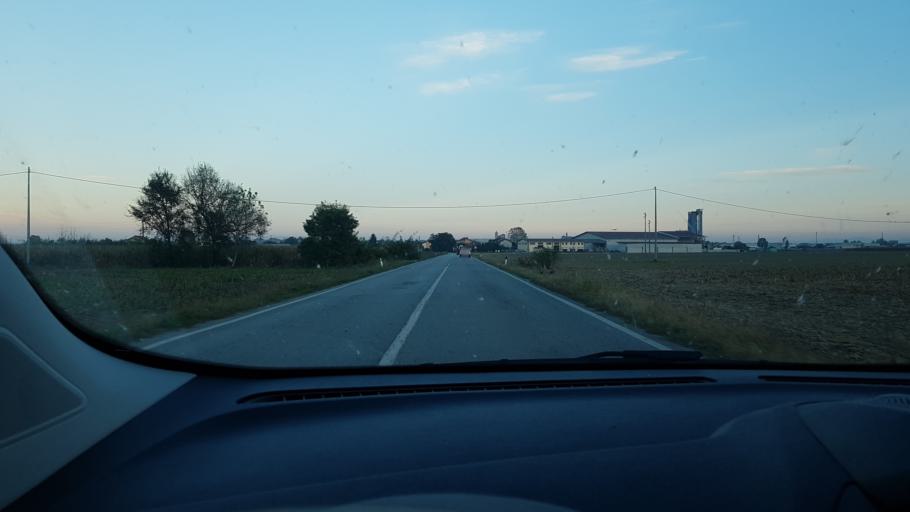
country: IT
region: Piedmont
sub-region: Provincia di Cuneo
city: Fossano
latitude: 44.5547
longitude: 7.6963
